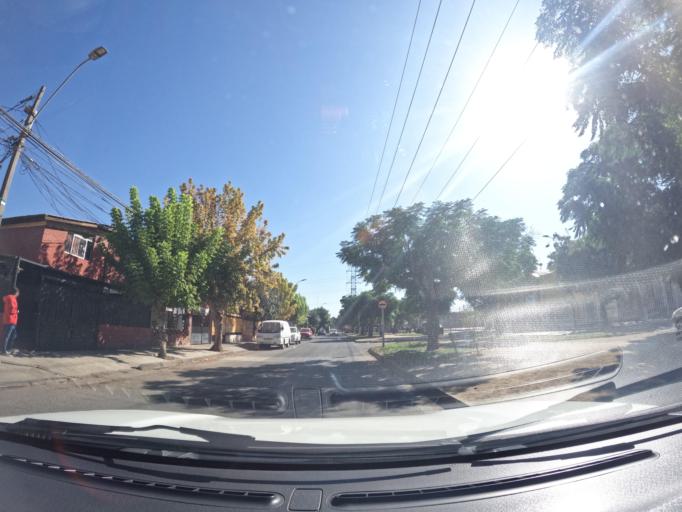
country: CL
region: Santiago Metropolitan
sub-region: Provincia de Santiago
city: Villa Presidente Frei, Nunoa, Santiago, Chile
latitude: -33.5040
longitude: -70.5744
